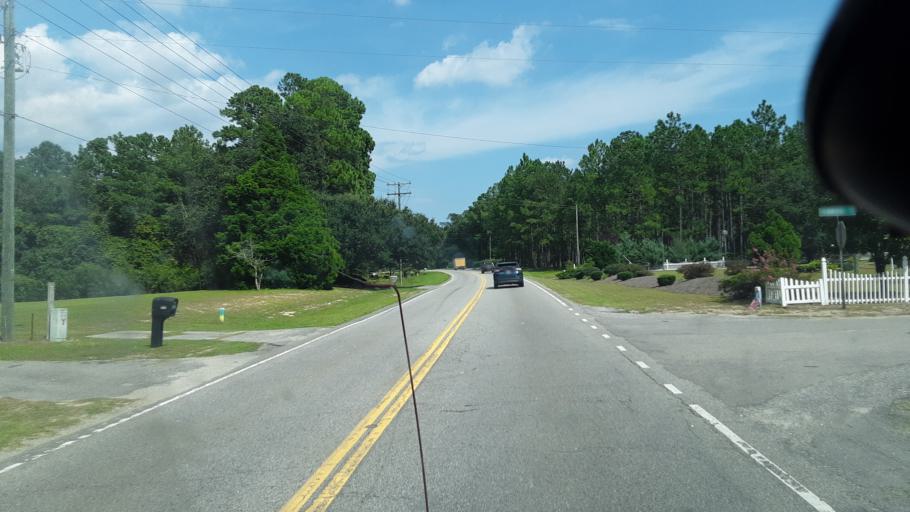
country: US
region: South Carolina
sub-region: Horry County
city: Red Hill
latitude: 33.8210
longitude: -78.9342
